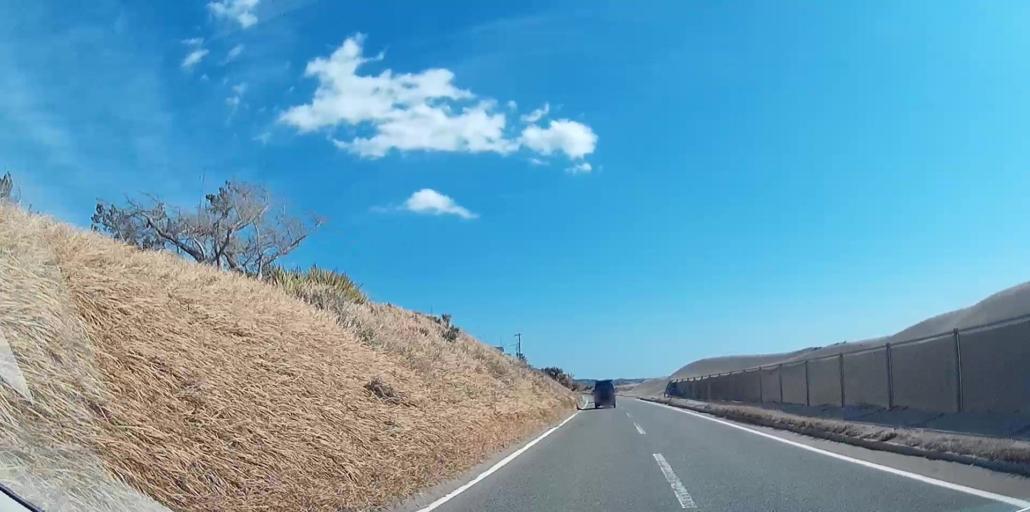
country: JP
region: Chiba
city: Tateyama
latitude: 34.9540
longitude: 139.7884
